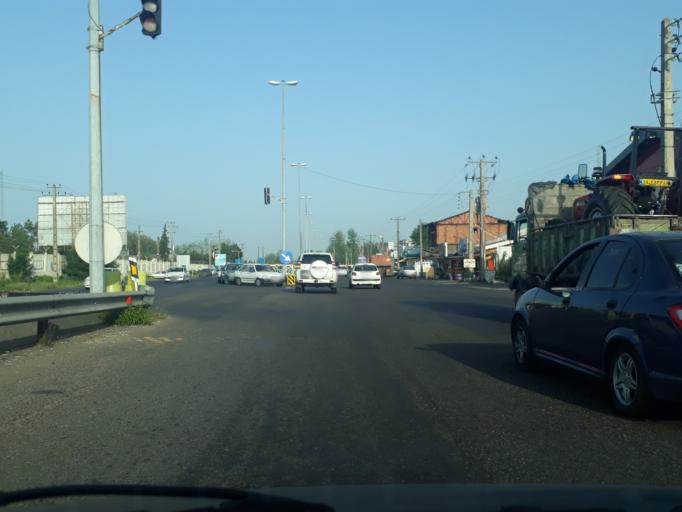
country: IR
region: Gilan
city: Bandar-e Anzali
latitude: 37.4575
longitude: 49.6093
